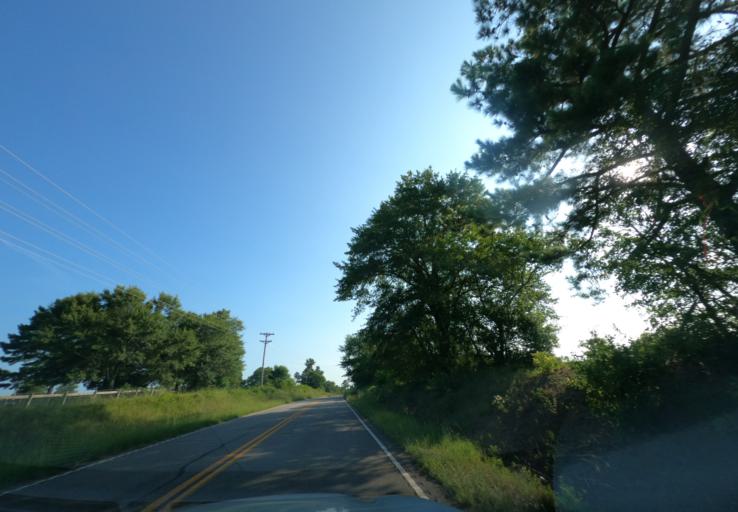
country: US
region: South Carolina
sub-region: Edgefield County
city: Murphys Estates
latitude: 33.5996
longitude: -81.9768
